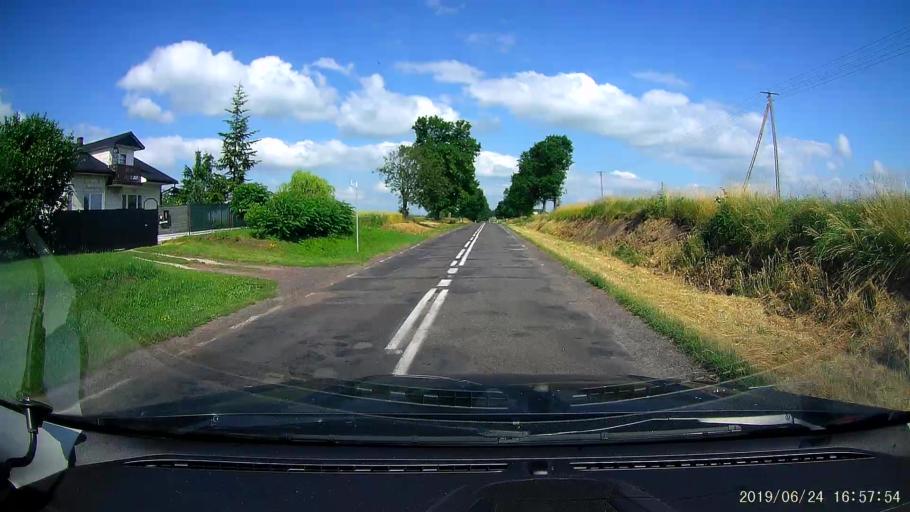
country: PL
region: Lublin Voivodeship
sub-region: Powiat tomaszowski
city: Telatyn
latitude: 50.5259
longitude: 23.8675
